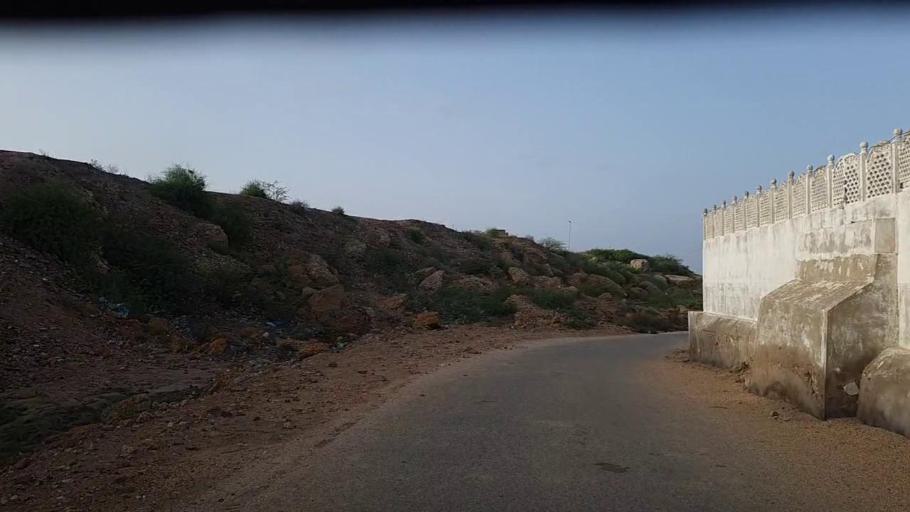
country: PK
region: Sindh
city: Thatta
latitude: 24.7520
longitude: 67.9002
